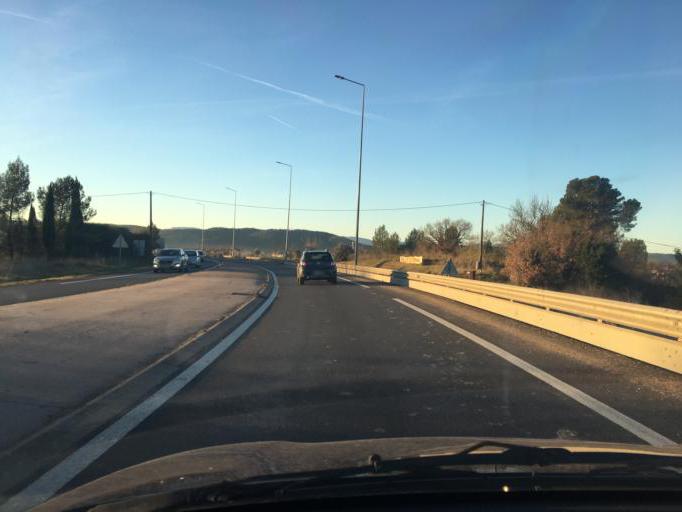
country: FR
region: Provence-Alpes-Cote d'Azur
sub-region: Departement du Var
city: Les Arcs
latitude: 43.4611
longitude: 6.4882
